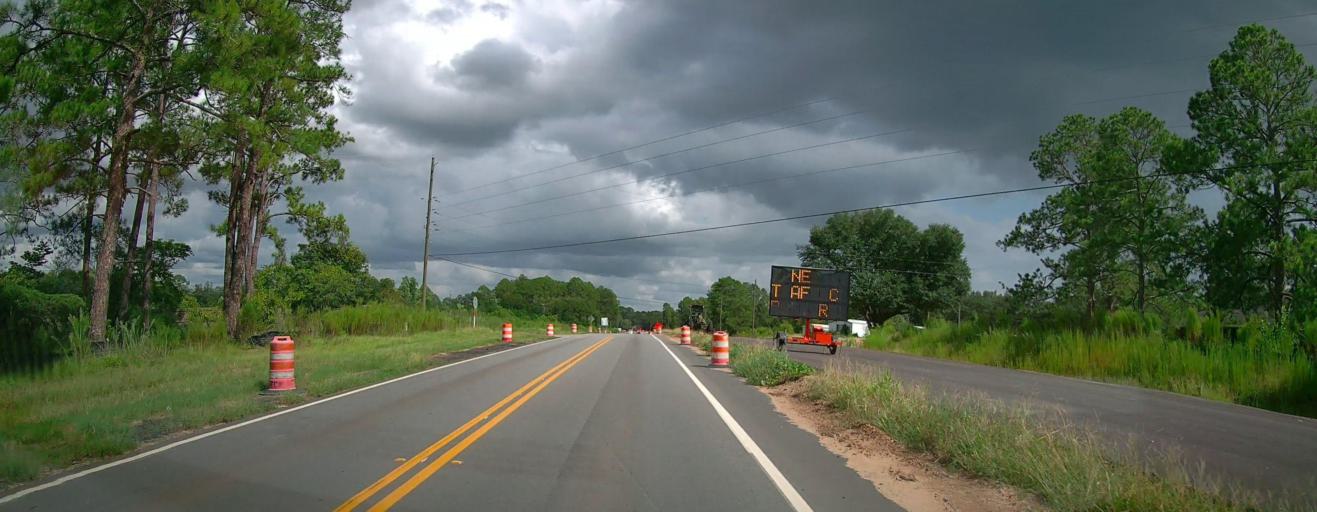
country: US
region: Georgia
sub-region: Coffee County
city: Douglas
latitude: 31.5308
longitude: -82.9114
